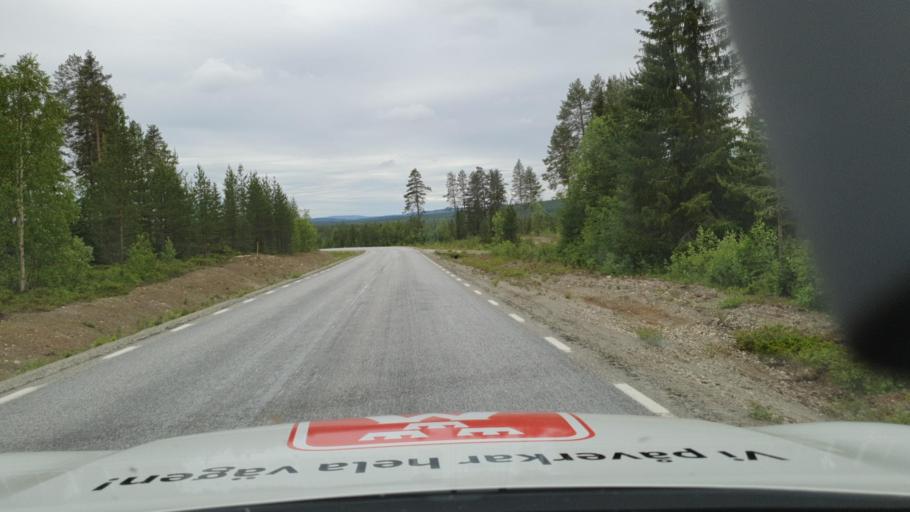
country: SE
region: Vaesterbotten
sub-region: Lycksele Kommun
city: Lycksele
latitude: 64.1301
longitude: 18.3602
